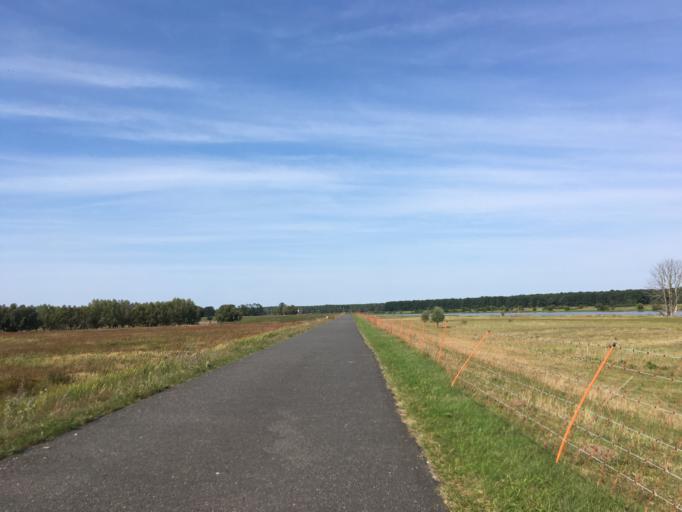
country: DE
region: Brandenburg
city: Neuzelle
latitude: 52.0775
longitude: 14.7447
